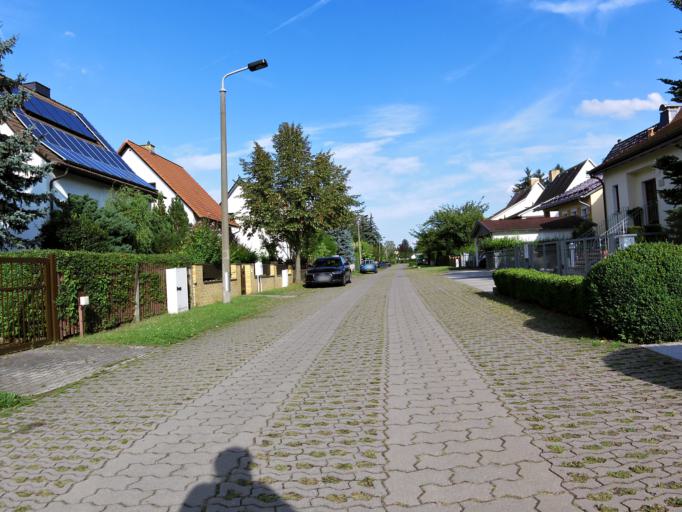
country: DE
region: Saxony
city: Taucha
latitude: 51.3487
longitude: 12.4604
